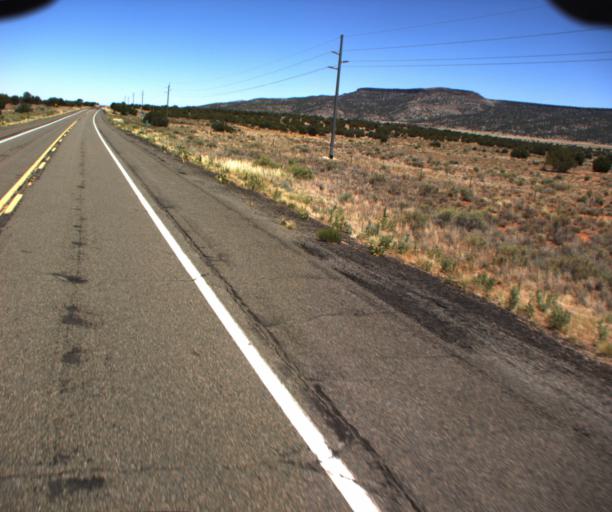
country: US
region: Arizona
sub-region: Coconino County
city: LeChee
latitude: 34.8284
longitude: -110.9541
